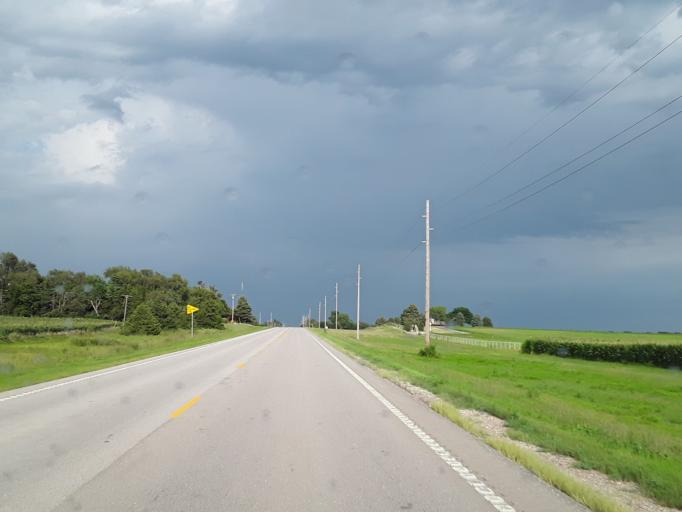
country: US
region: Nebraska
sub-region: Saunders County
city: Ashland
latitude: 41.0887
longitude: -96.4032
